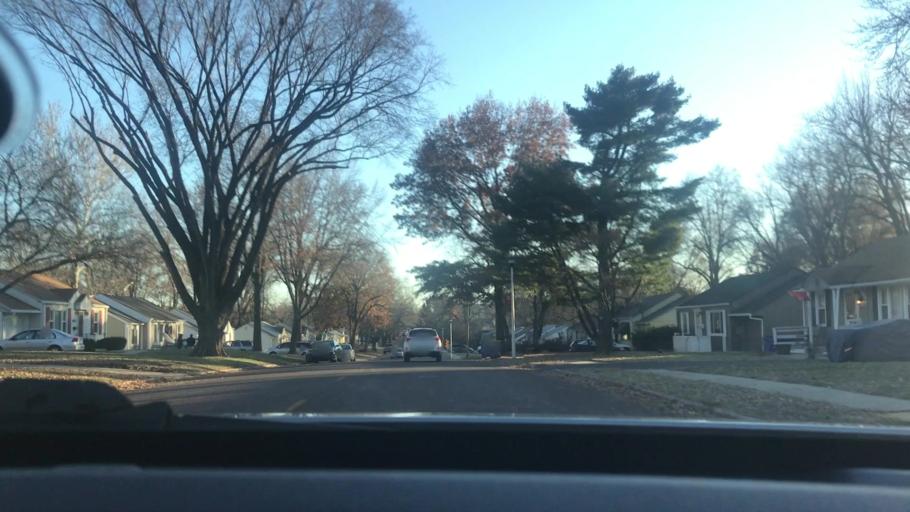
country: US
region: Kansas
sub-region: Johnson County
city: Overland Park
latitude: 38.9905
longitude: -94.6735
